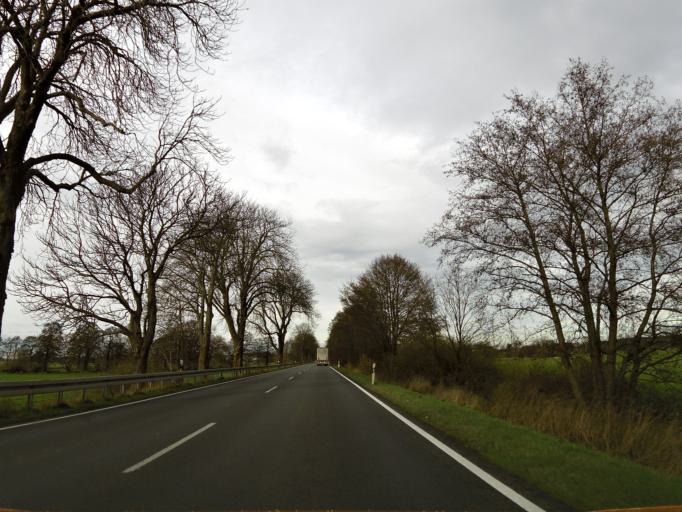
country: DE
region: Saxony-Anhalt
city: Klotze
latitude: 52.6914
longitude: 11.2630
